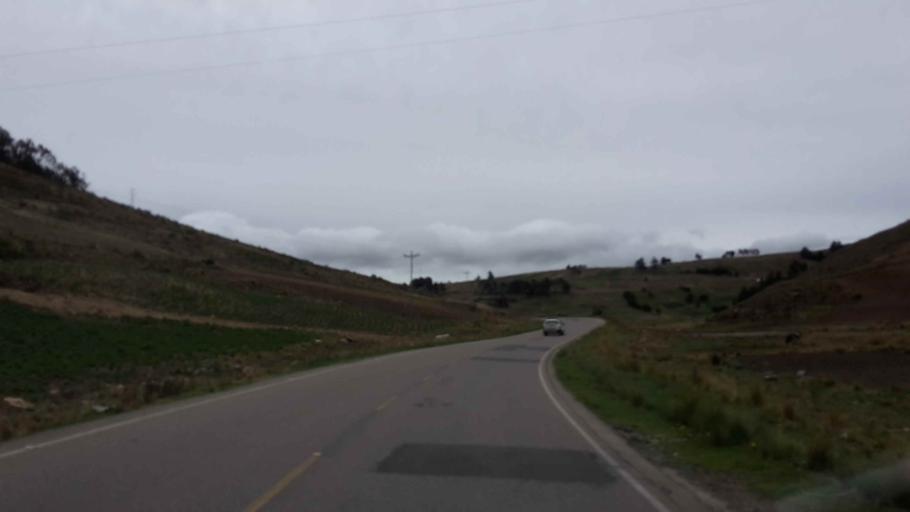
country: BO
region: Cochabamba
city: Arani
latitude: -17.4802
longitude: -65.5918
